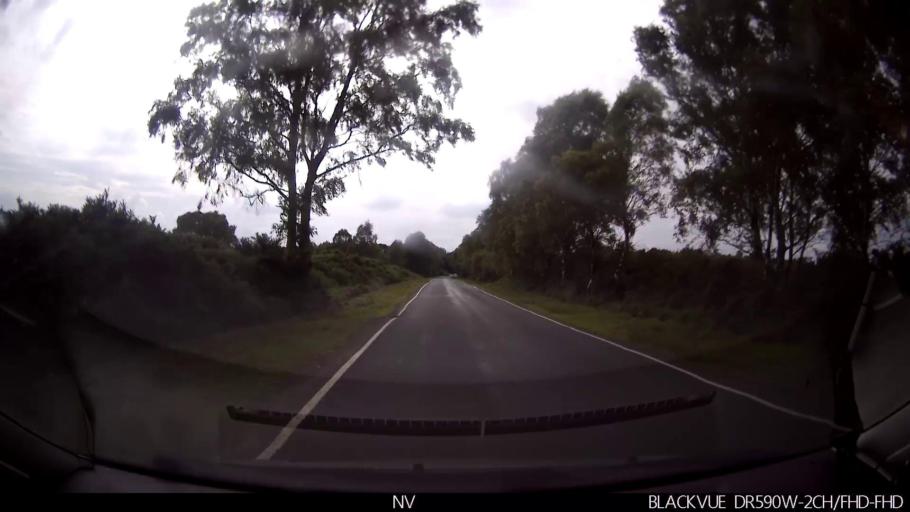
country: GB
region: England
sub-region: North Yorkshire
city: Strensall
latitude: 54.0475
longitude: -1.0003
